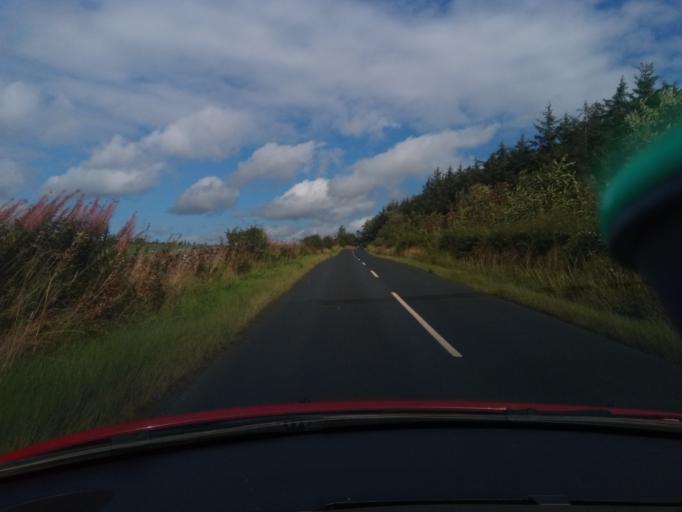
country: GB
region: Scotland
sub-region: The Scottish Borders
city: Melrose
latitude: 55.5725
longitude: -2.7320
